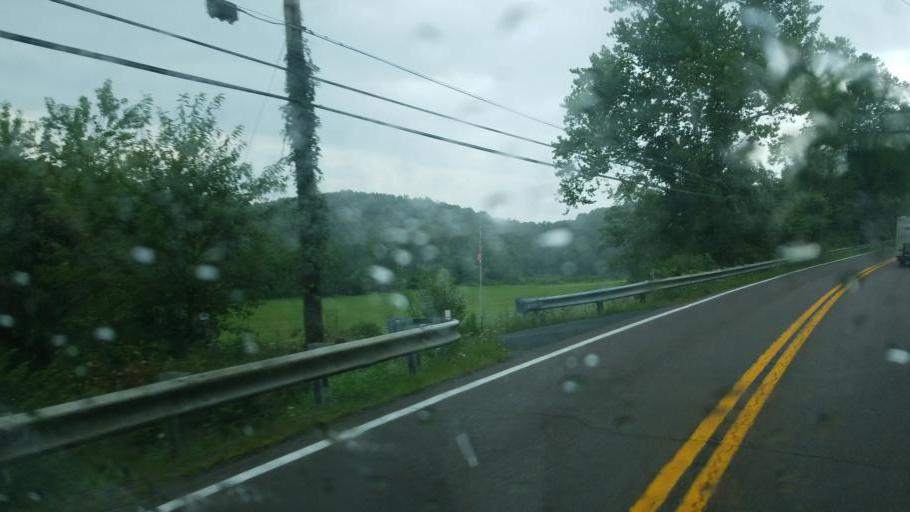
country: US
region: West Virginia
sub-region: Mineral County
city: Fort Ashby
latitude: 39.5424
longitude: -78.5734
